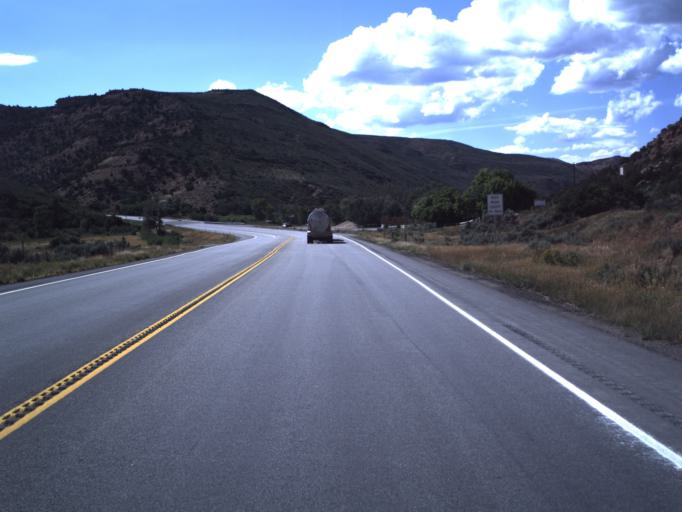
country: US
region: Utah
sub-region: Duchesne County
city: Duchesne
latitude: 40.1994
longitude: -110.9022
